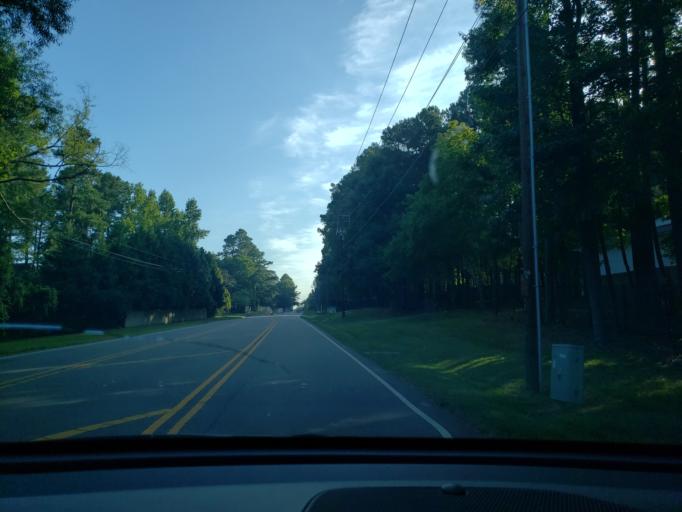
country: US
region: North Carolina
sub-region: Durham County
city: Durham
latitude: 35.9236
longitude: -78.9562
